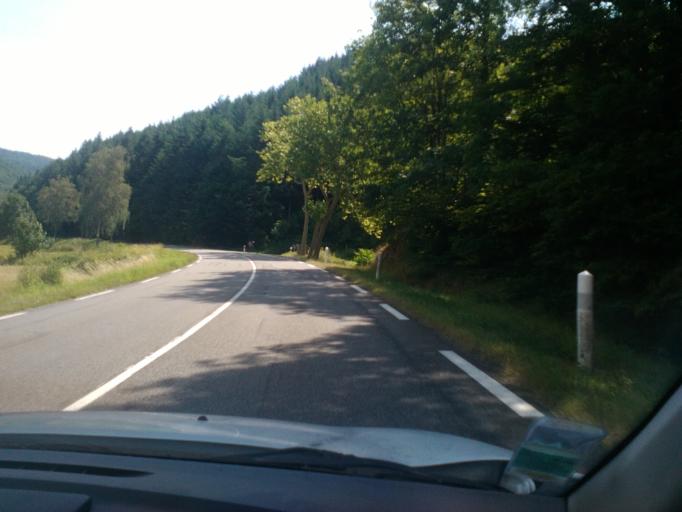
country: FR
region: Alsace
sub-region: Departement du Haut-Rhin
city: Freland
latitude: 48.1533
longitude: 7.2077
